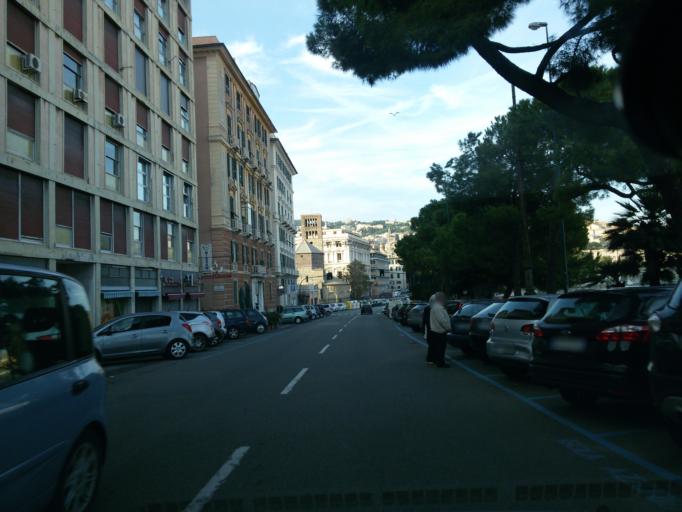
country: IT
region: Liguria
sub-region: Provincia di Genova
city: San Teodoro
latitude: 44.4047
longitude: 8.9394
